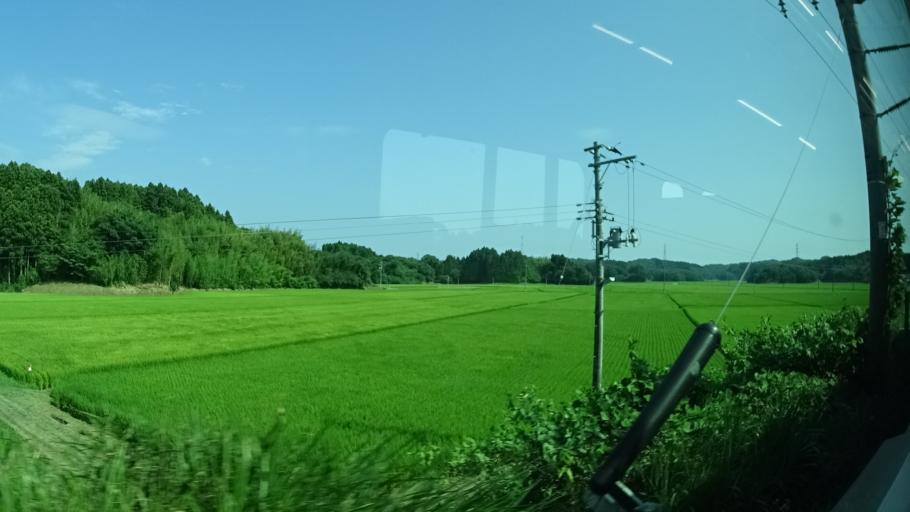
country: JP
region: Miyagi
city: Matsushima
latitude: 38.4352
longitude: 141.0851
